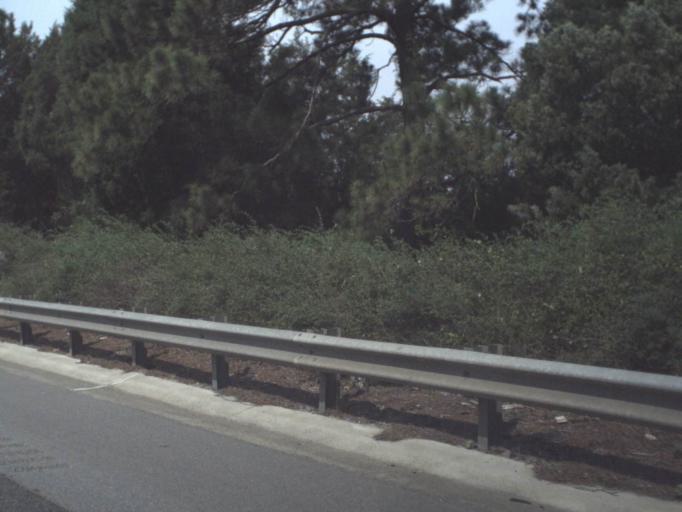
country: US
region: Georgia
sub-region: Camden County
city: Kingsland
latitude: 30.7411
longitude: -81.6561
